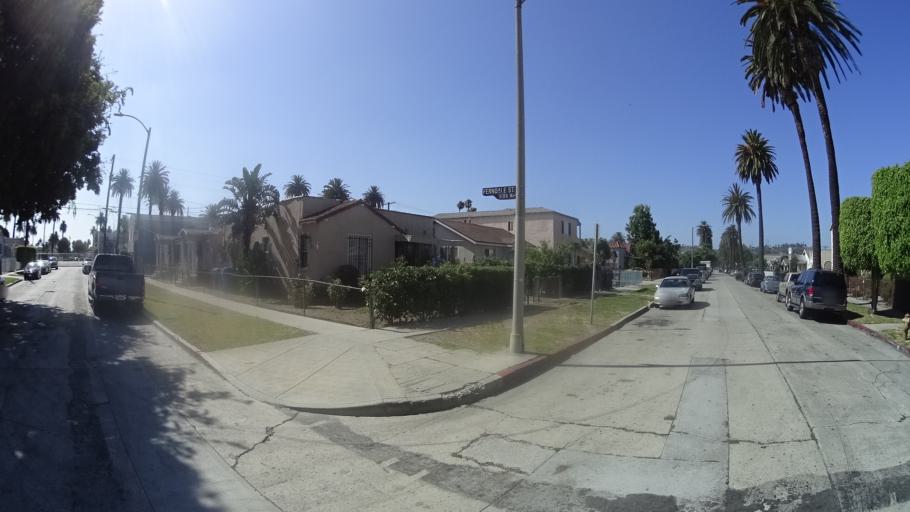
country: US
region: California
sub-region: Los Angeles County
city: View Park-Windsor Hills
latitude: 34.0316
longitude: -118.3557
